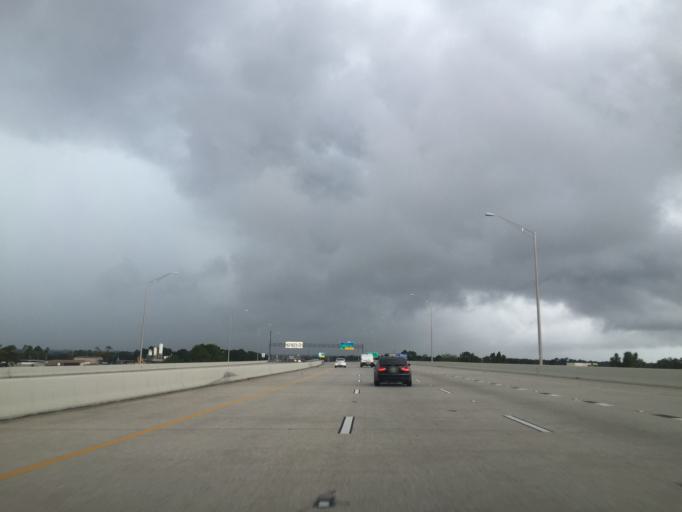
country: US
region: Florida
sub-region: Orange County
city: Lockhart
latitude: 28.6340
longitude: -81.4628
